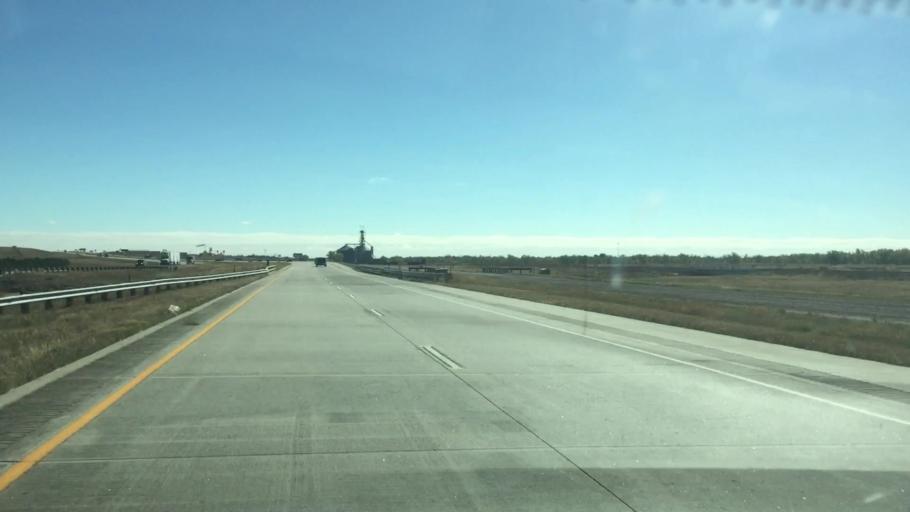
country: US
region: Colorado
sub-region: Lincoln County
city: Limon
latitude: 39.2742
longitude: -103.7402
